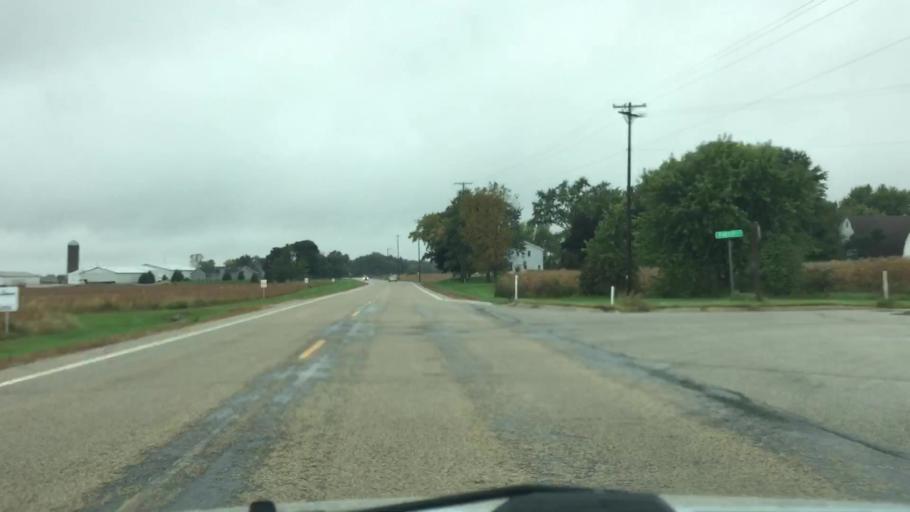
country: US
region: Wisconsin
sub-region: Jefferson County
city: Palmyra
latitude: 42.8788
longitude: -88.6301
